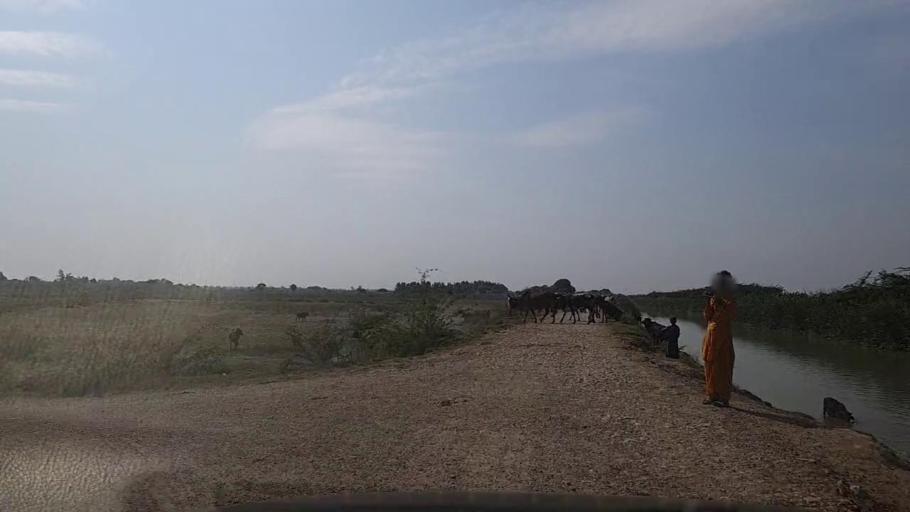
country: PK
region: Sindh
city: Thatta
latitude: 24.7667
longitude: 67.7977
